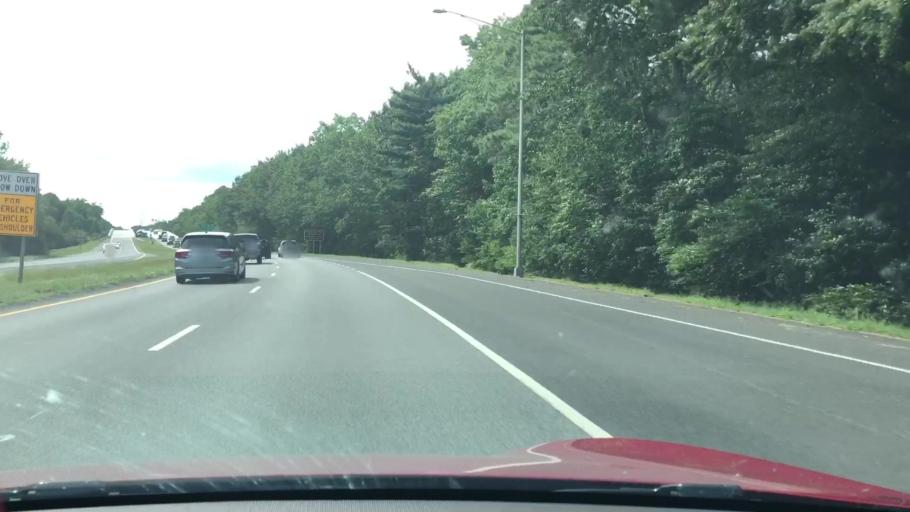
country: US
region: Maryland
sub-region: Worcester County
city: Pocomoke City
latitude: 38.0790
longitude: -75.5642
